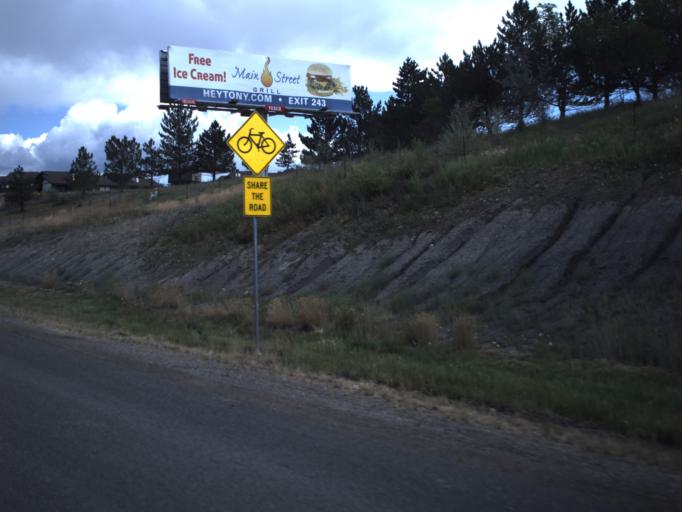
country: US
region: Utah
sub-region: Carbon County
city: Wellington
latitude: 39.5450
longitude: -110.7452
